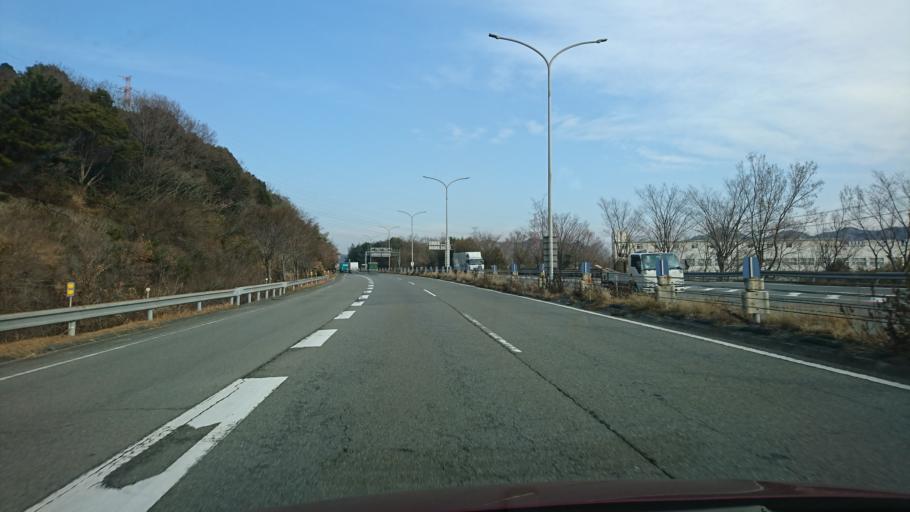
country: JP
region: Hyogo
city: Shirahamacho-usazakiminami
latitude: 34.8032
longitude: 134.7435
